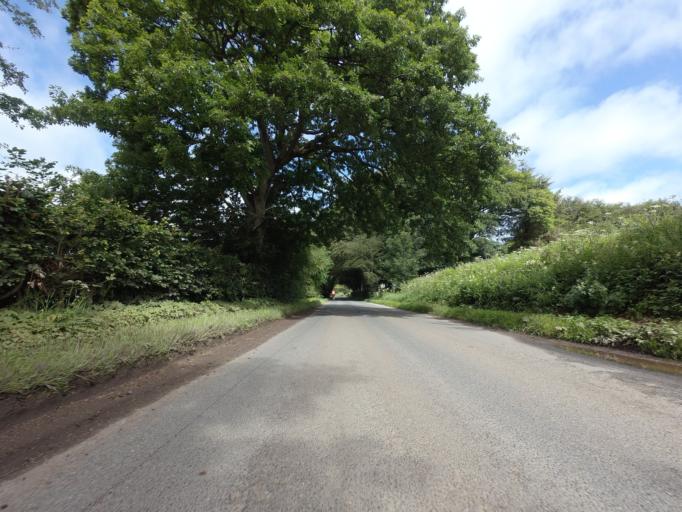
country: GB
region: Scotland
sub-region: Aberdeenshire
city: Turriff
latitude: 57.5471
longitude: -2.4816
